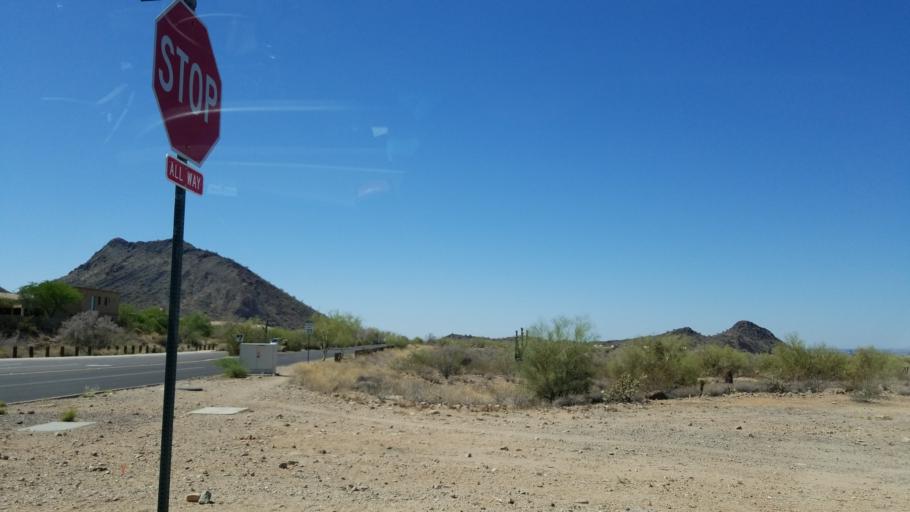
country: US
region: Arizona
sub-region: Maricopa County
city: Fountain Hills
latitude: 33.5896
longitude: -111.7876
